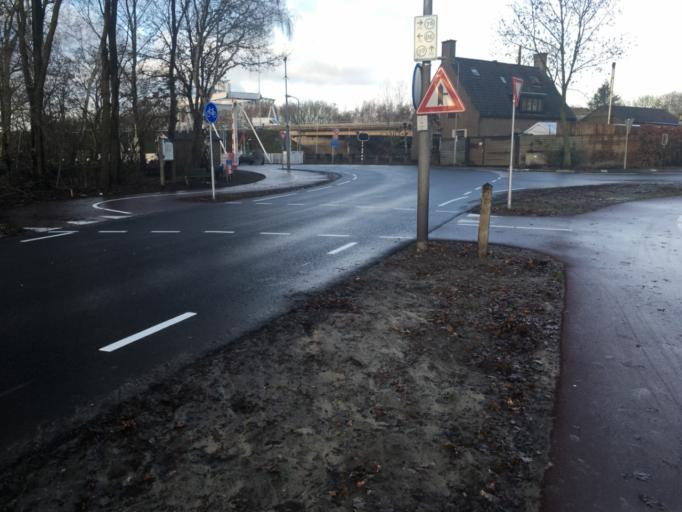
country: NL
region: North Brabant
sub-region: Gemeente Tilburg
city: Tilburg
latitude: 51.5460
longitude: 5.1196
